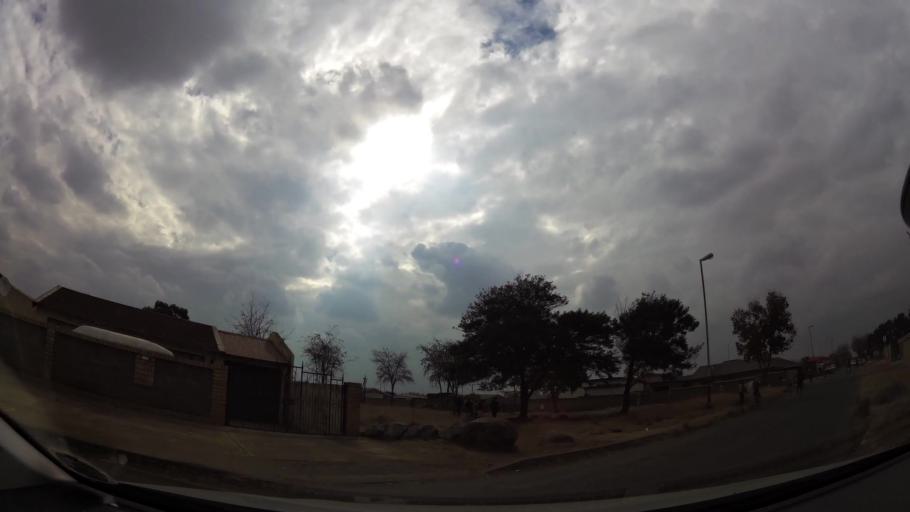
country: ZA
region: Gauteng
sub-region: City of Johannesburg Metropolitan Municipality
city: Soweto
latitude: -26.2635
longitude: 27.8514
